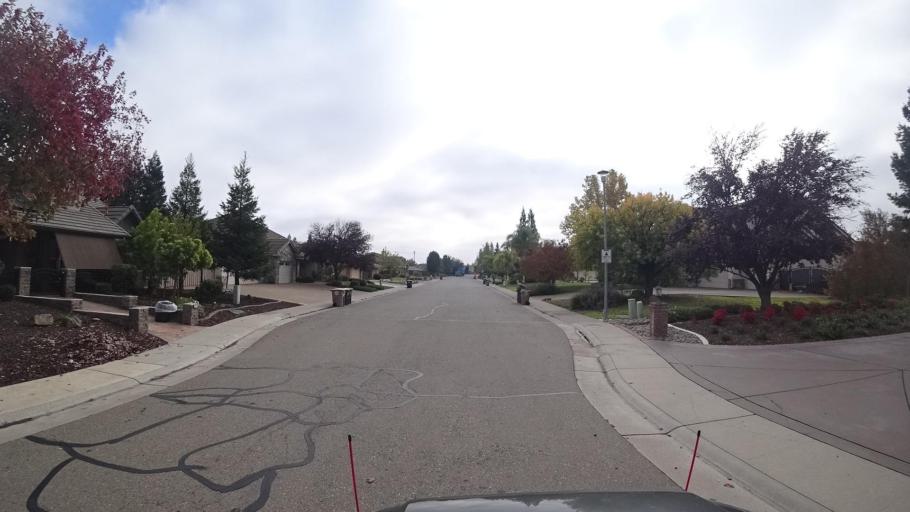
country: US
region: California
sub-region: Sacramento County
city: Elk Grove
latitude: 38.4255
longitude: -121.3692
